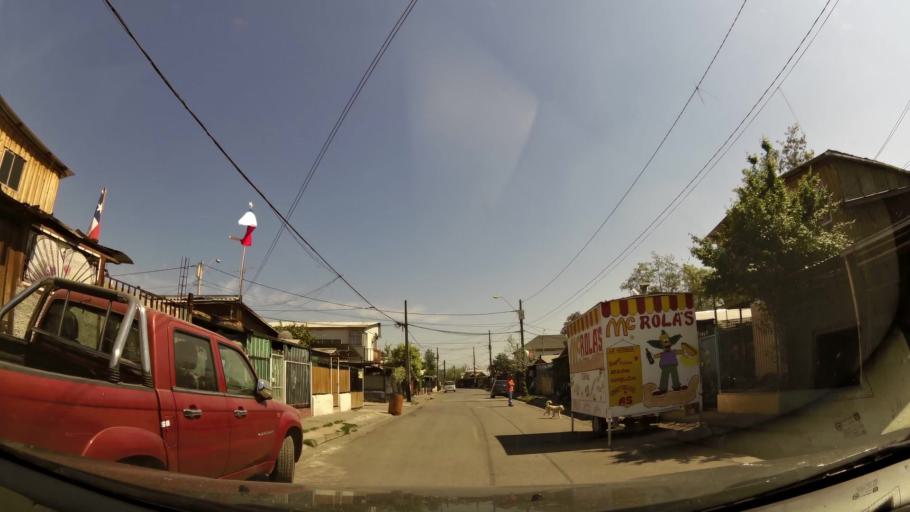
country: CL
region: Santiago Metropolitan
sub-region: Provincia de Santiago
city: La Pintana
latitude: -33.5887
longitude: -70.6253
